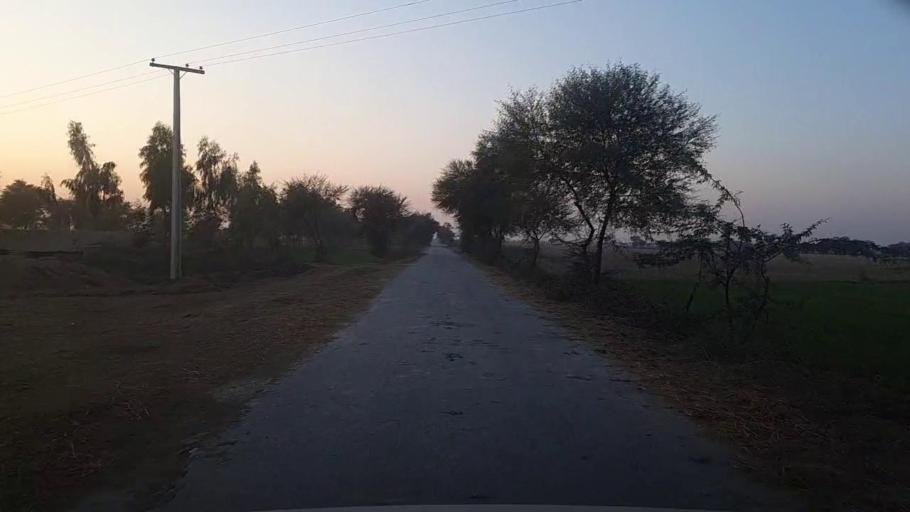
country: PK
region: Sindh
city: Khairpur Nathan Shah
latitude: 27.1577
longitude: 67.7154
